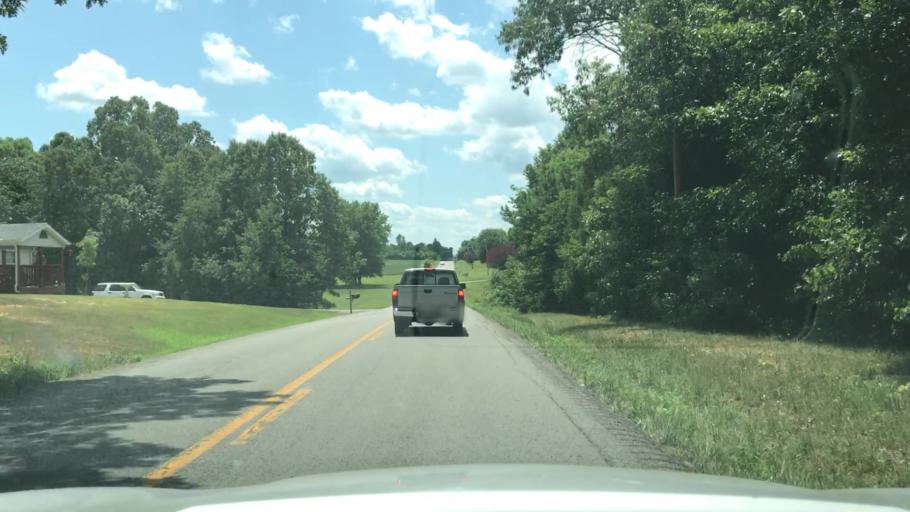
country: US
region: Kentucky
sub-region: Muhlenberg County
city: Greenville
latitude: 37.1726
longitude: -87.2430
